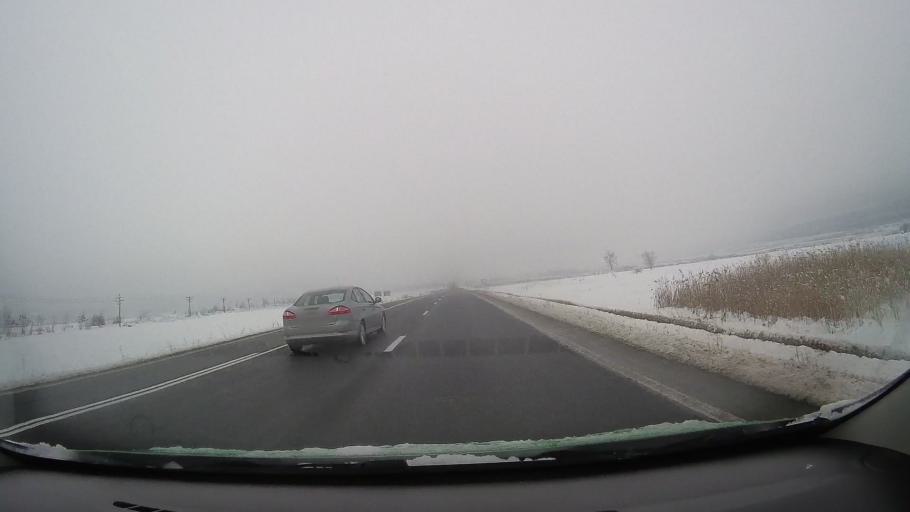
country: RO
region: Sibiu
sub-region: Oras Saliste
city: Saliste
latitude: 45.7929
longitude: 23.9177
